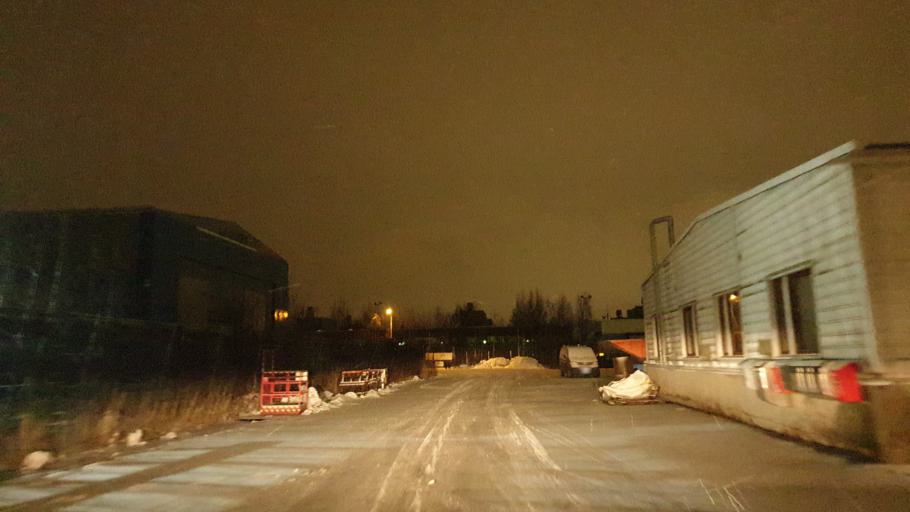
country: FI
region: Northern Ostrobothnia
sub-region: Oulu
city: Oulu
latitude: 64.9926
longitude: 25.4543
